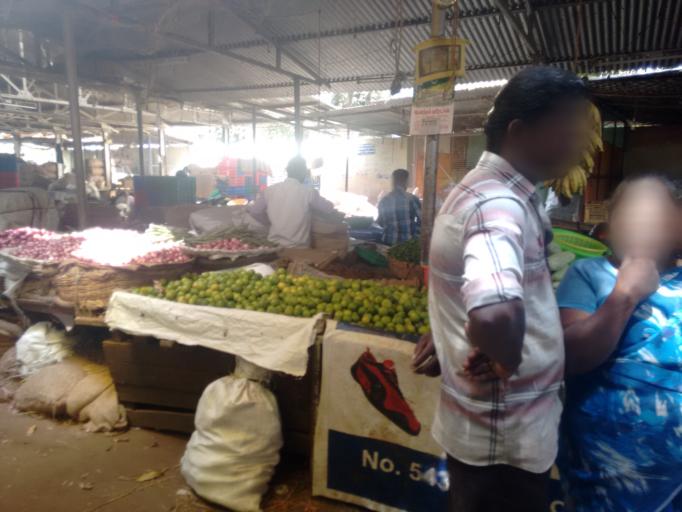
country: IN
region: Tamil Nadu
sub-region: Coimbatore
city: Coimbatore
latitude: 10.9900
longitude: 76.9598
